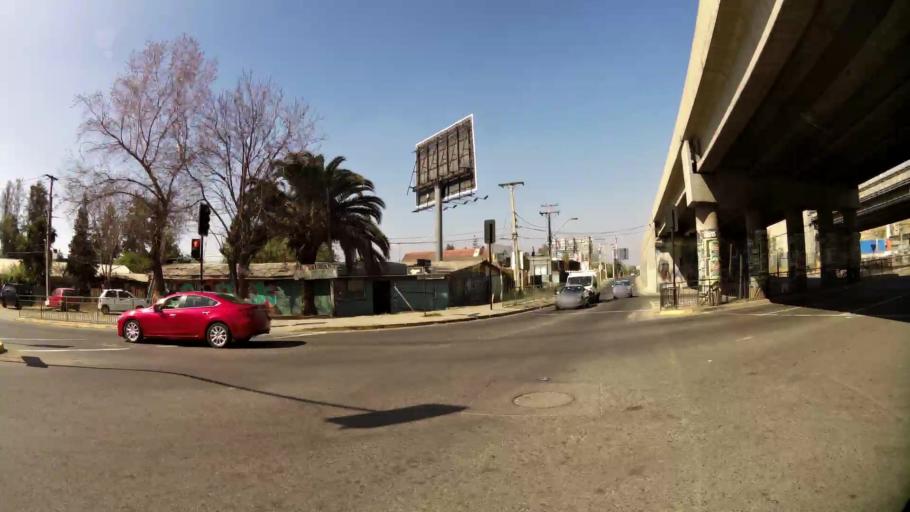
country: CL
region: Santiago Metropolitan
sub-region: Provincia de Santiago
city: Lo Prado
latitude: -33.3717
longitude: -70.7385
